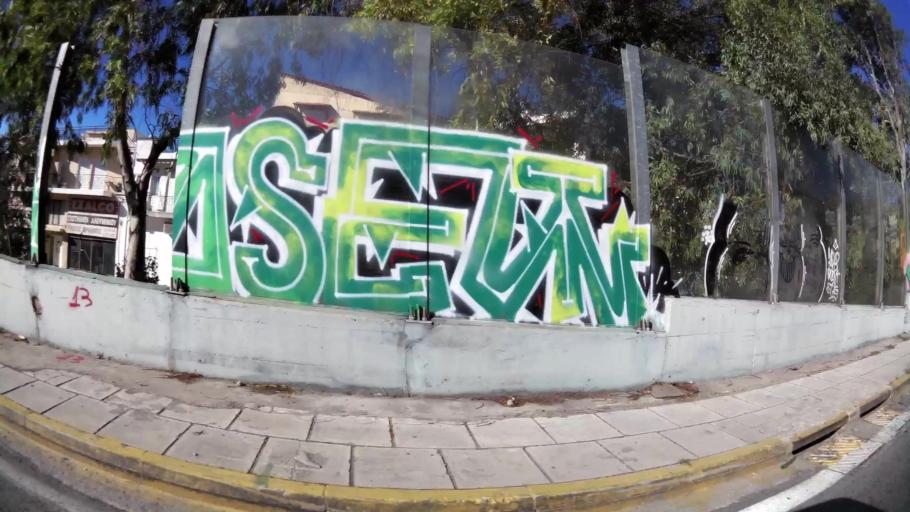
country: GR
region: Attica
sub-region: Nomos Piraios
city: Keratsini
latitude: 37.9658
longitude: 23.6084
